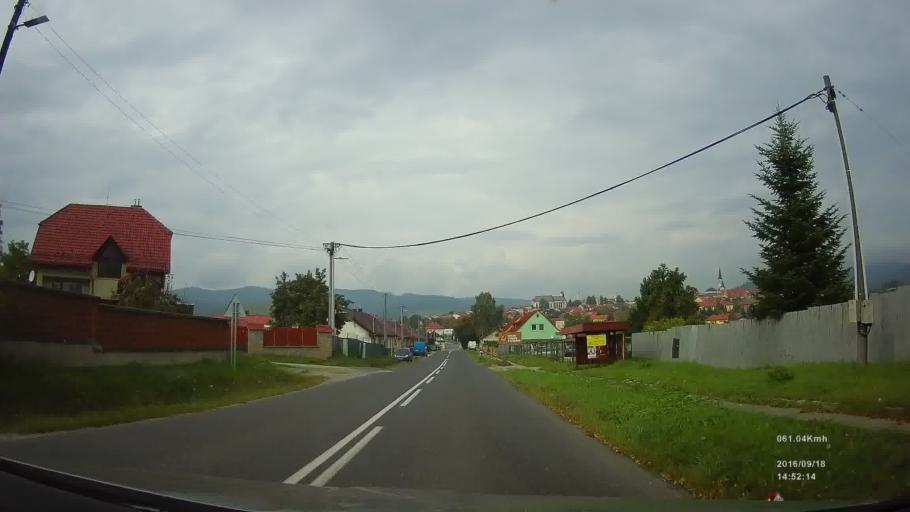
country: SK
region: Presovsky
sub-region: Okres Presov
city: Levoca
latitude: 49.0160
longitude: 20.5867
